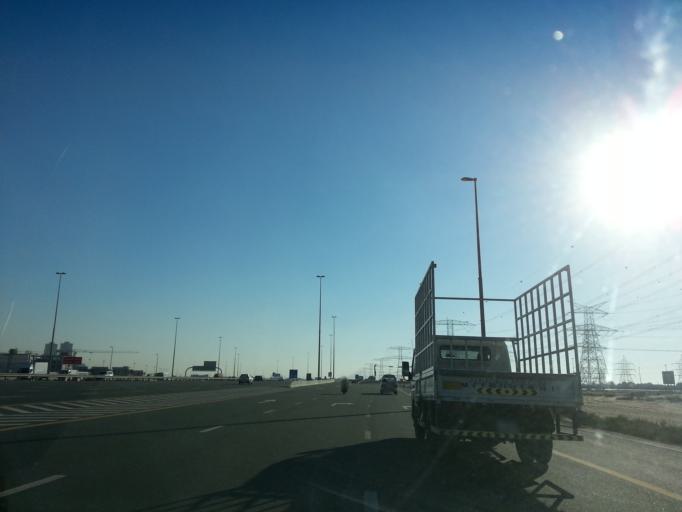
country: AE
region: Dubai
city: Dubai
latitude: 25.0657
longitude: 55.2001
